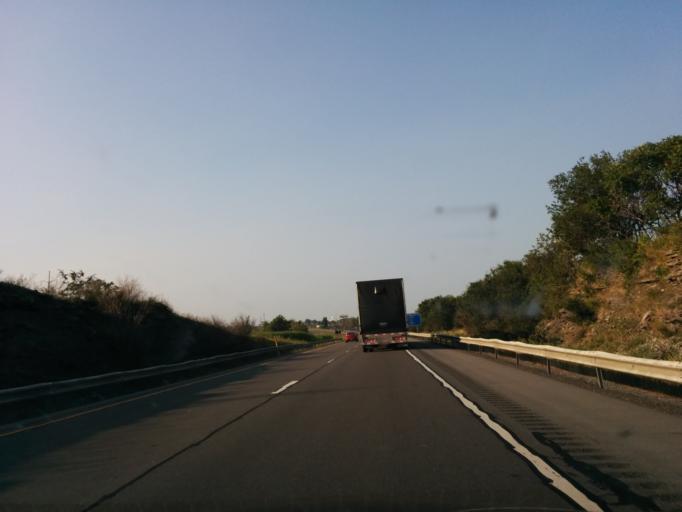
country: US
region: New York
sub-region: Jefferson County
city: Watertown
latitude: 43.9617
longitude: -75.9509
